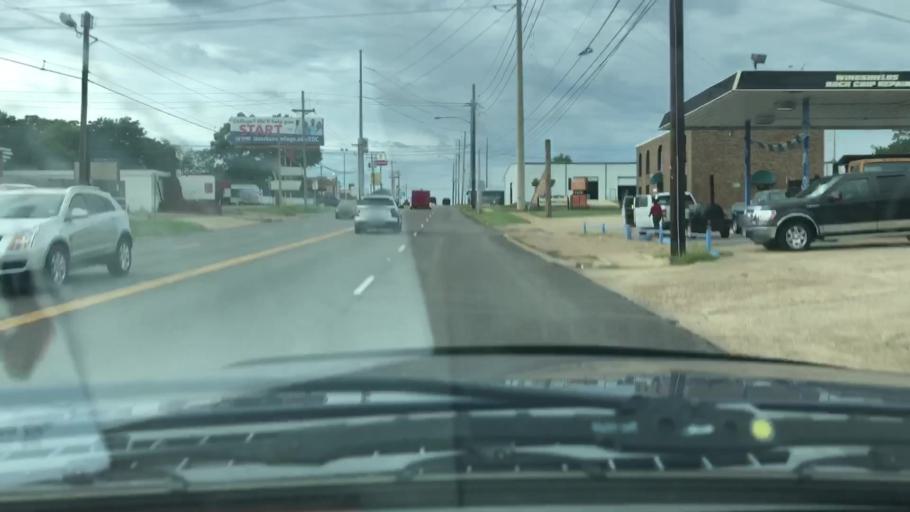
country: US
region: Texas
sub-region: Bowie County
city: Texarkana
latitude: 33.4351
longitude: -94.0581
